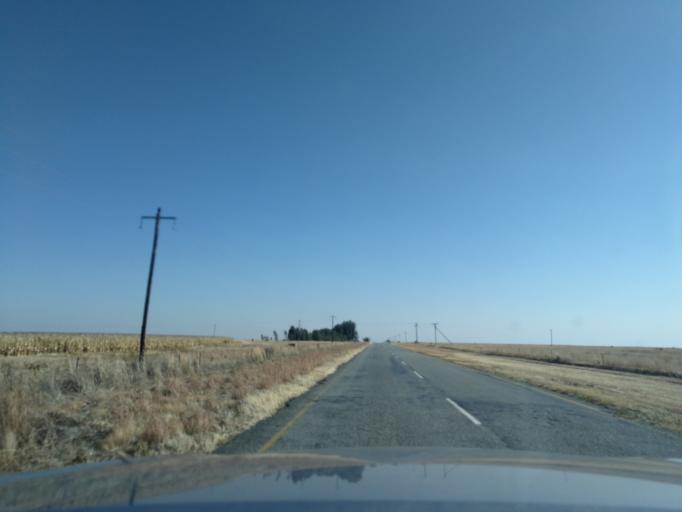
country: ZA
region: Orange Free State
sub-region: Fezile Dabi District Municipality
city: Viljoenskroon
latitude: -27.3801
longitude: 27.0451
